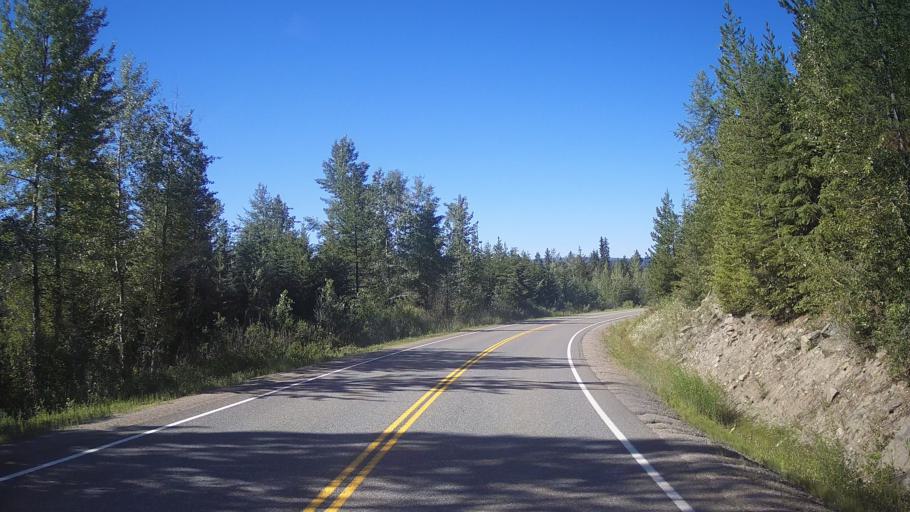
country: CA
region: British Columbia
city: Kamloops
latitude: 51.4795
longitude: -120.4687
